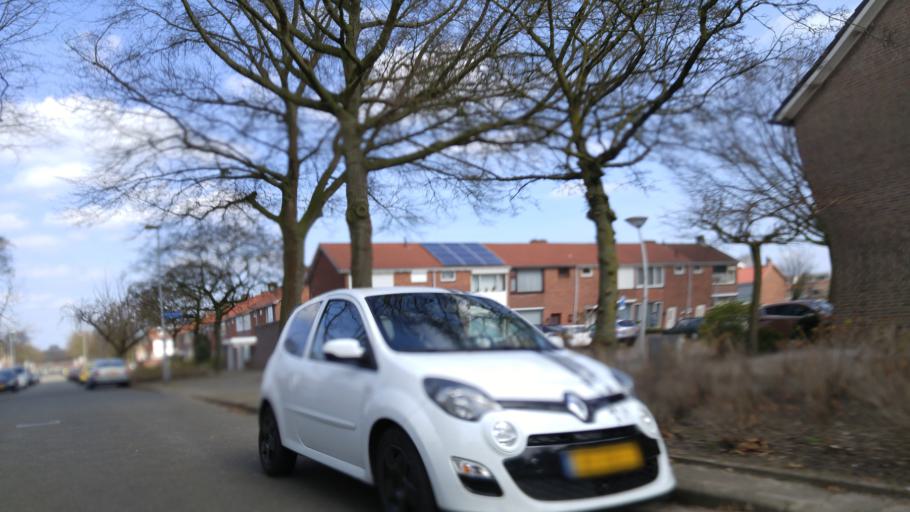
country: NL
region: North Brabant
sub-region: Gemeente Eindhoven
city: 't Hofke
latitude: 51.4738
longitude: 5.4981
